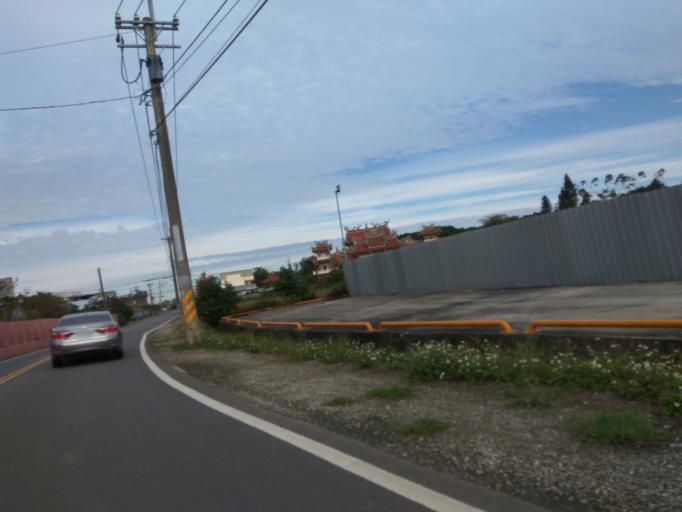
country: TW
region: Taiwan
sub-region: Hsinchu
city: Zhubei
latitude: 24.9589
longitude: 121.1183
